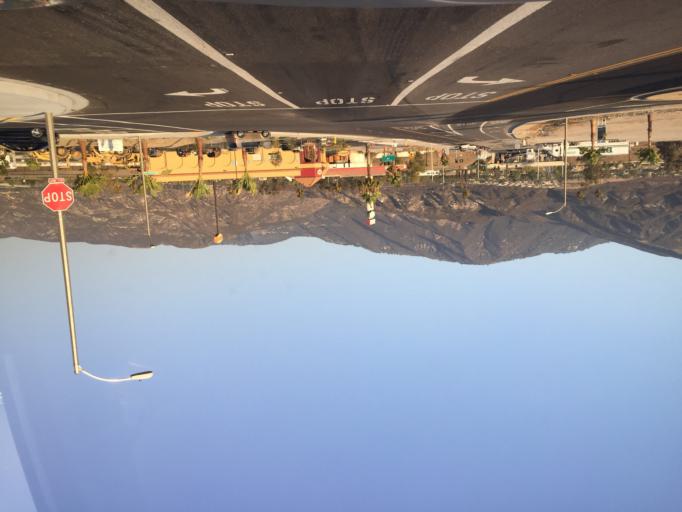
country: US
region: California
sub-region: San Bernardino County
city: Muscoy
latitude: 34.1887
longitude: -117.3631
